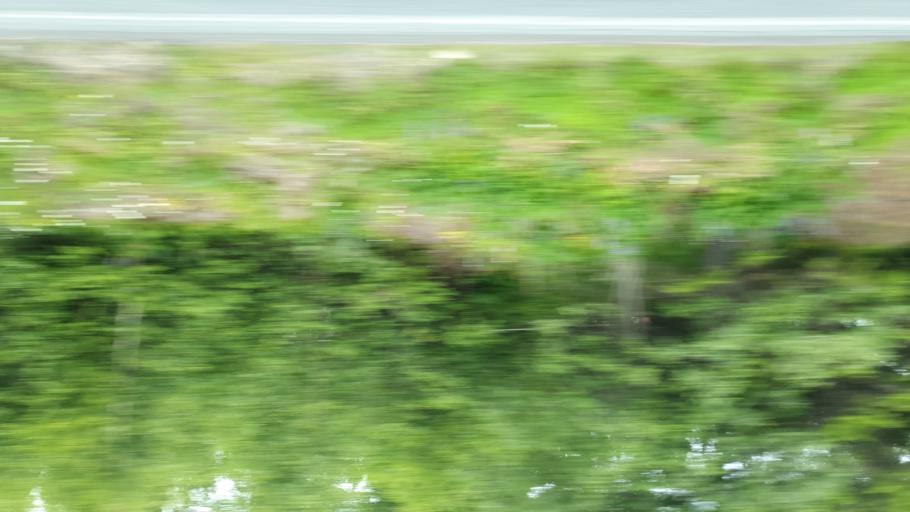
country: NO
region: Sor-Trondelag
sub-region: Rennebu
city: Berkak
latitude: 62.8484
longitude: 10.0187
